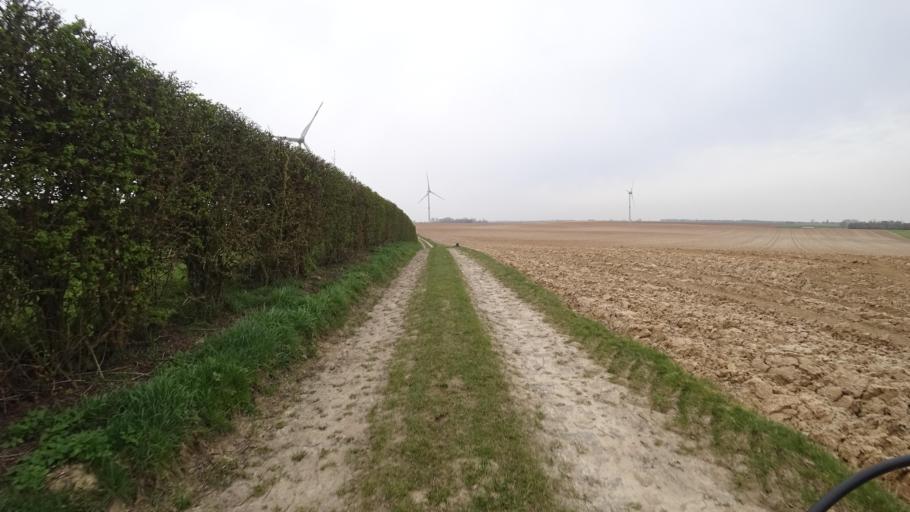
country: BE
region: Wallonia
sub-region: Province du Brabant Wallon
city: Walhain-Saint-Paul
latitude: 50.5971
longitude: 4.7047
